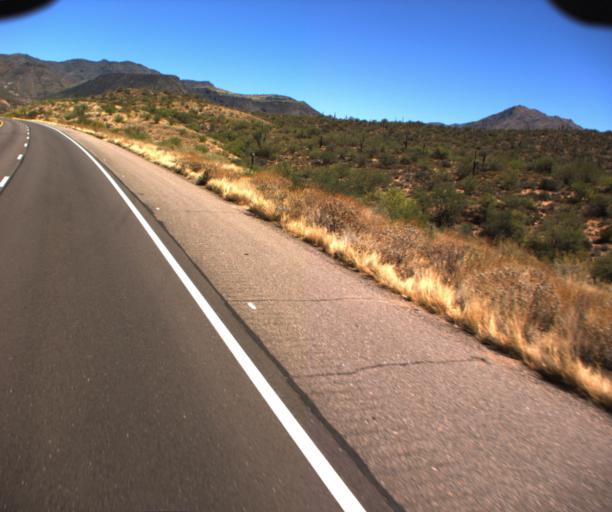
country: US
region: Arizona
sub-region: Maricopa County
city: Rio Verde
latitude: 33.7853
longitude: -111.4929
